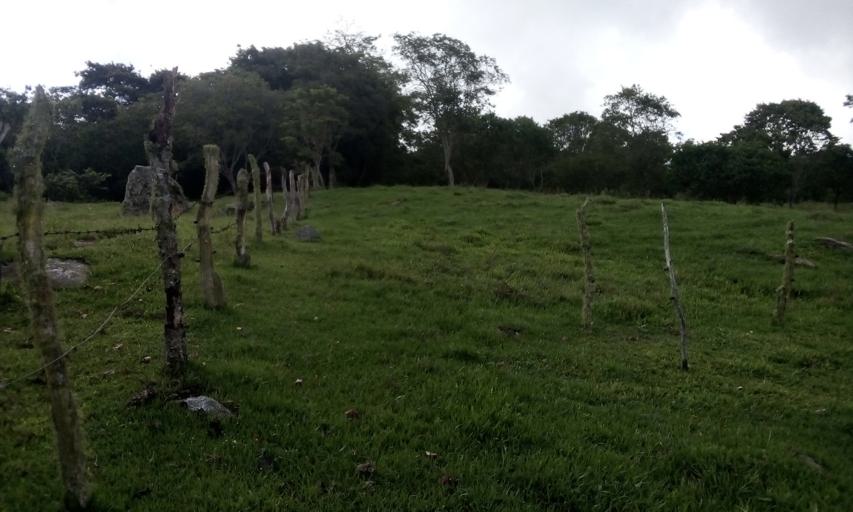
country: CO
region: Boyaca
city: Santana
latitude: 6.0049
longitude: -73.4943
